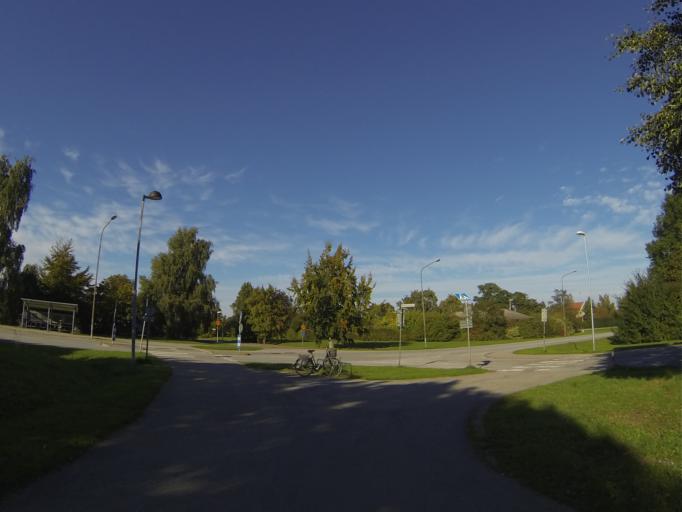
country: SE
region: Skane
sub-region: Lunds Kommun
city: Genarp
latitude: 55.7135
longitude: 13.3414
